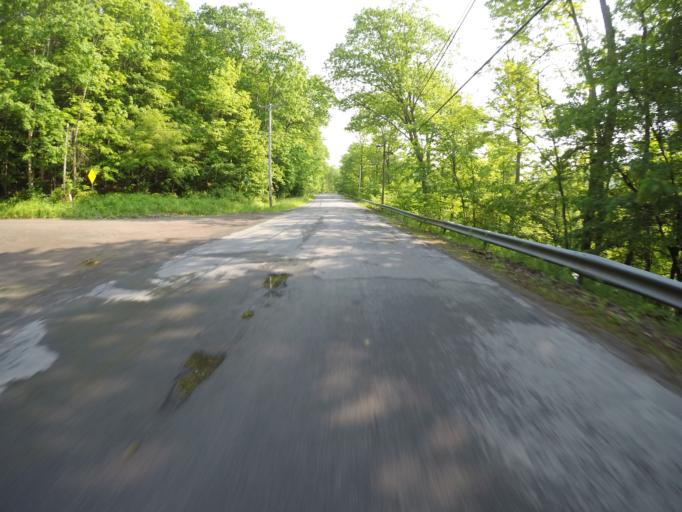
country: US
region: New York
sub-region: Delaware County
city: Stamford
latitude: 42.1412
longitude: -74.6575
